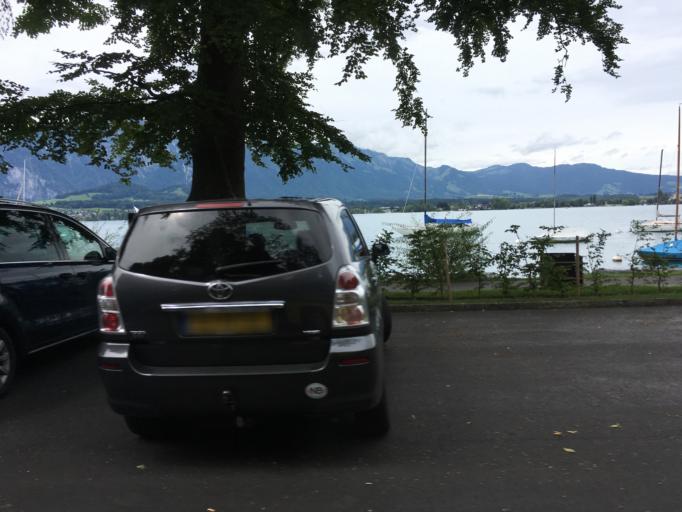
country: CH
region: Bern
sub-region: Thun District
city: Hilterfingen
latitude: 46.7384
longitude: 7.6538
